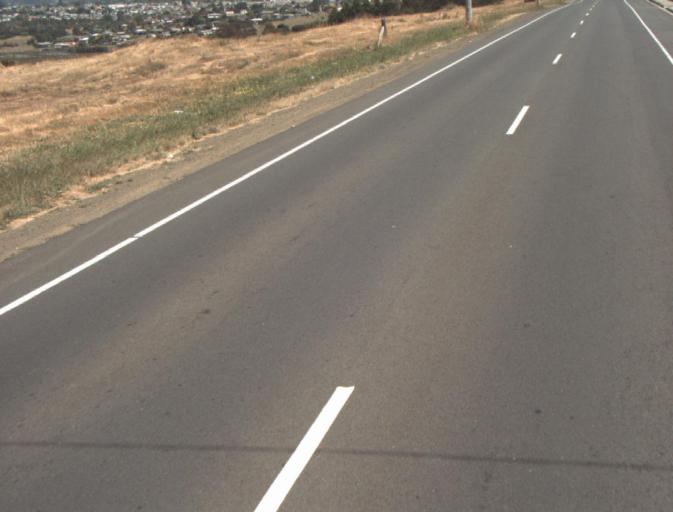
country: AU
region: Tasmania
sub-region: Launceston
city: Newstead
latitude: -41.4179
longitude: 147.1644
